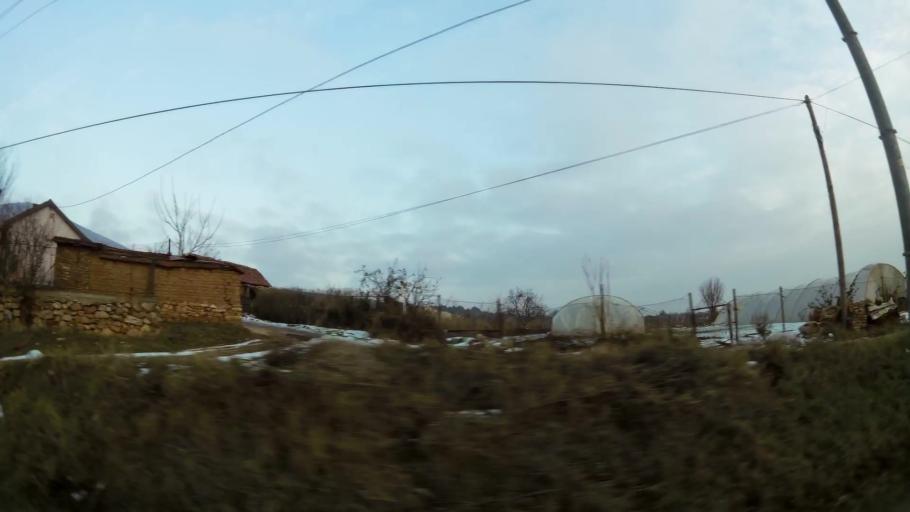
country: MK
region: Aracinovo
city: Arachinovo
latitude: 42.0321
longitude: 21.5484
